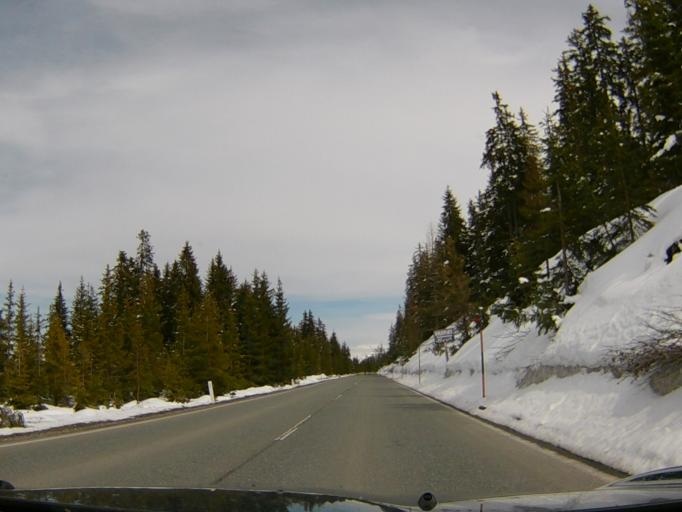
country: AT
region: Salzburg
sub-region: Politischer Bezirk Zell am See
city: Krimml
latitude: 47.2393
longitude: 12.1488
